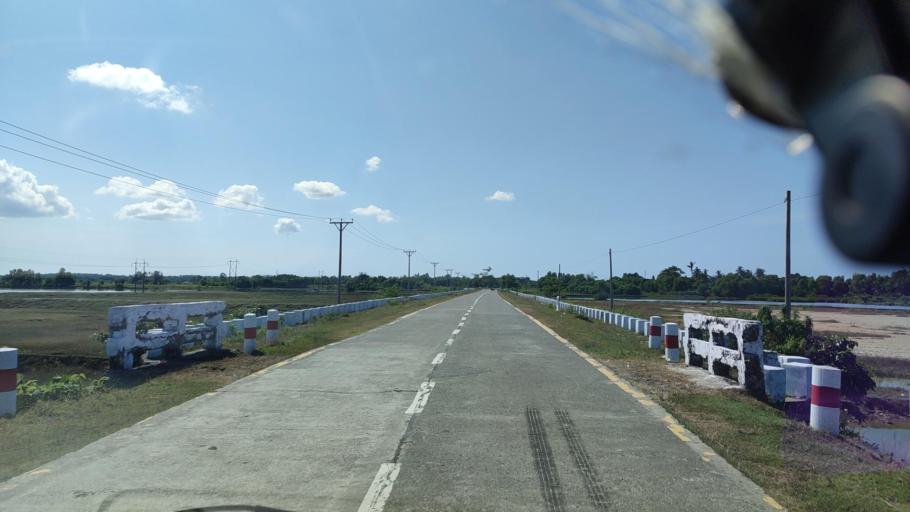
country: MM
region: Rakhine
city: Sittwe
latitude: 20.2914
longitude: 92.8773
